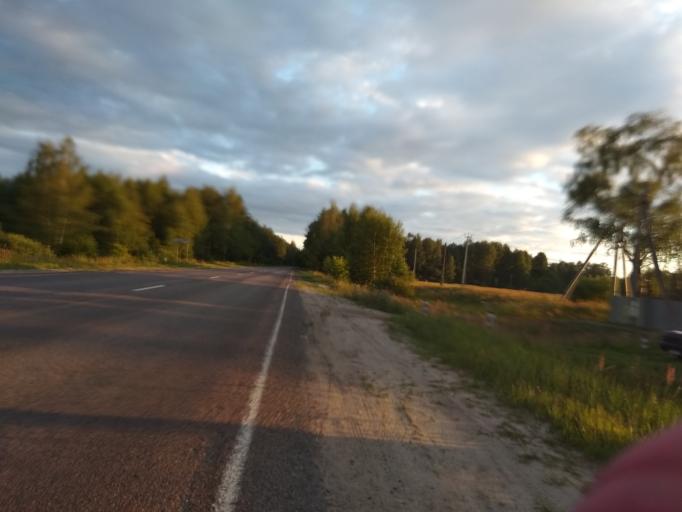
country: RU
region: Moskovskaya
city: Kerva
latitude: 55.5842
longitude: 39.6967
